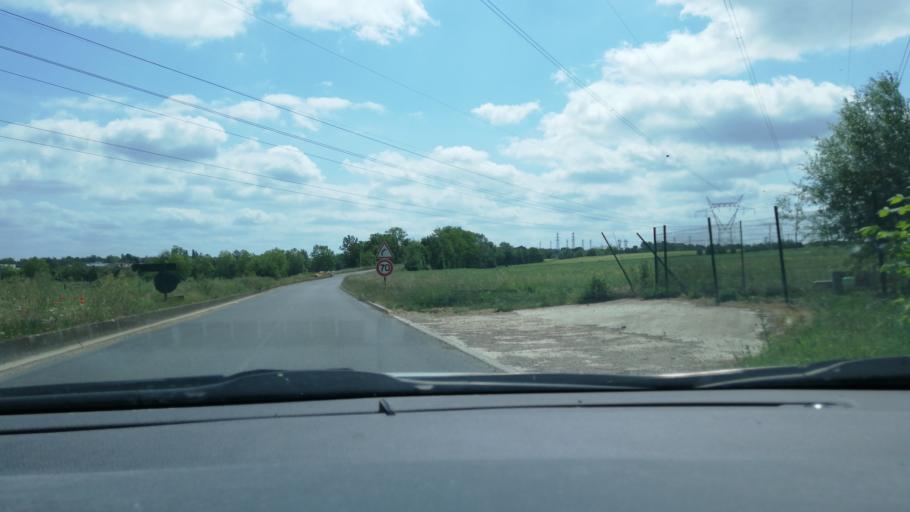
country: FR
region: Ile-de-France
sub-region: Departement du Val-d'Oise
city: Vaureal
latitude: 49.0639
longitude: 2.0213
